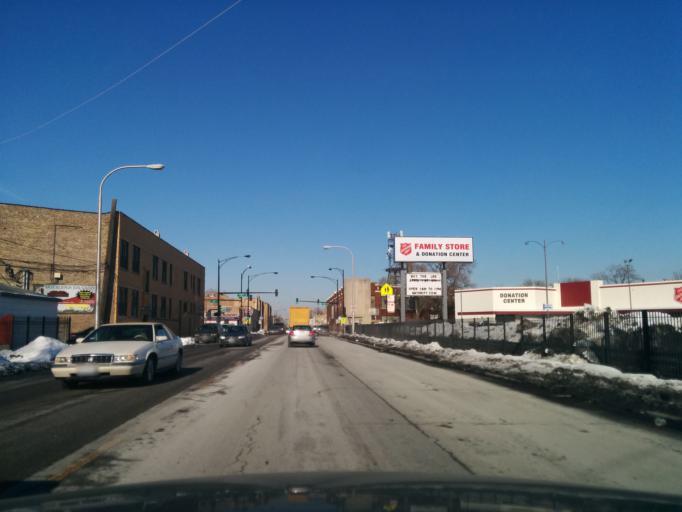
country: US
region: Illinois
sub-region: Cook County
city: Oak Park
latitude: 41.9068
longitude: -87.7278
